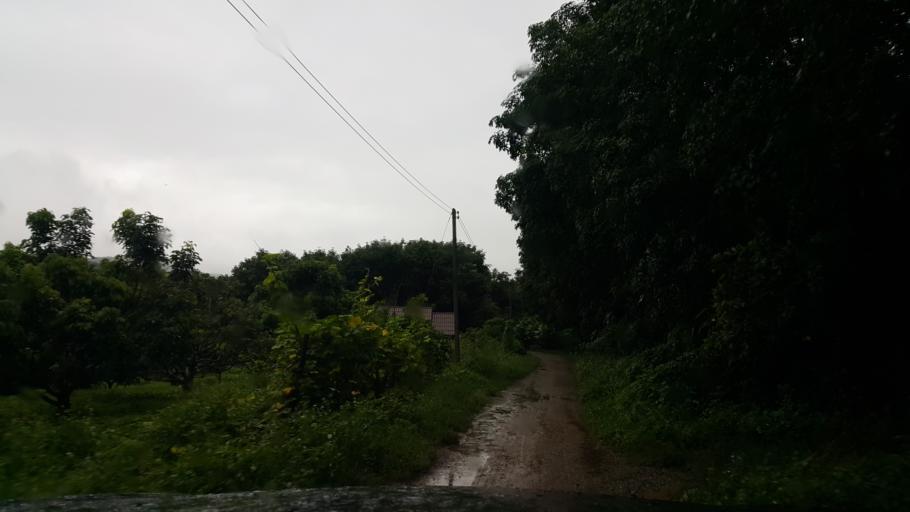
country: TH
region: Phayao
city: Phu Sang
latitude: 19.6185
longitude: 100.4060
